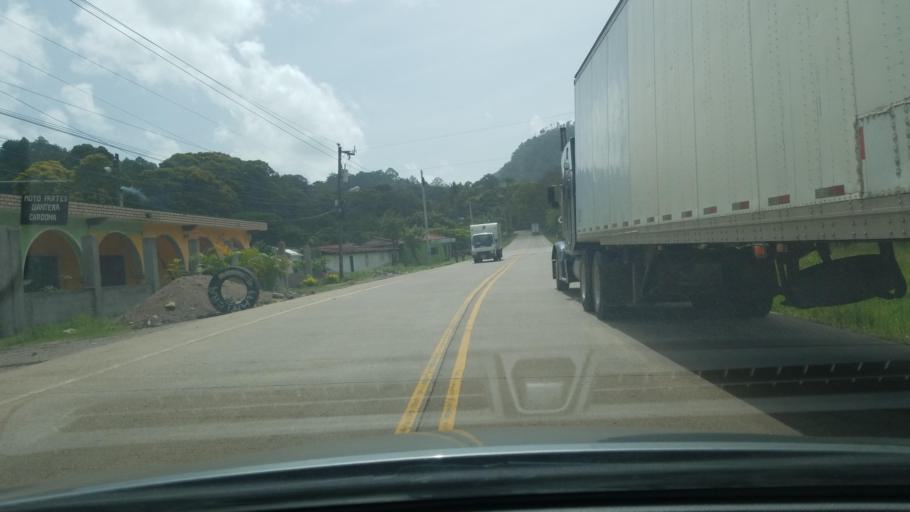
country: HN
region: Copan
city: San Agustin
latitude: 14.9179
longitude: -88.9863
